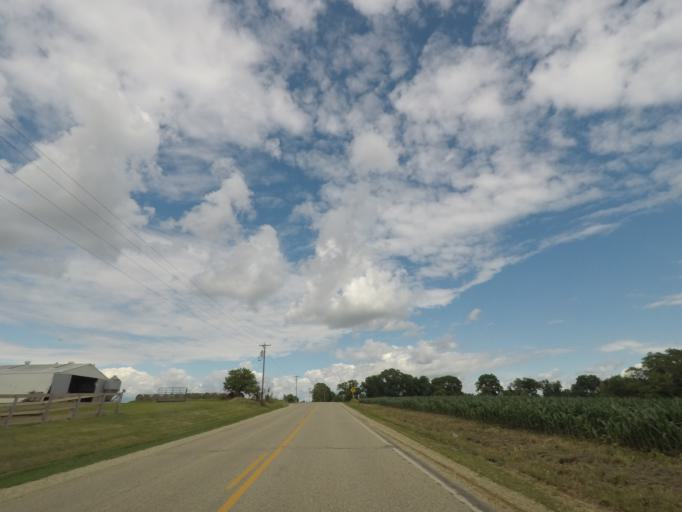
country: US
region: Wisconsin
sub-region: Rock County
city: Evansville
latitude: 42.7157
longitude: -89.2425
